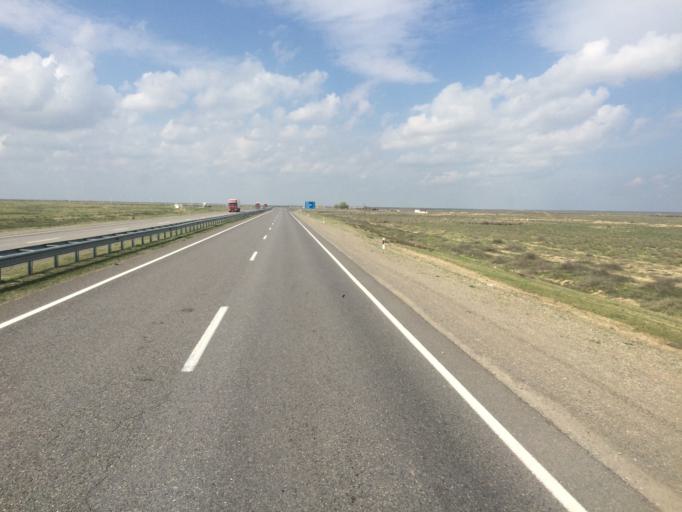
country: KZ
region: Ongtustik Qazaqstan
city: Turkestan
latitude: 43.5297
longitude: 67.7856
